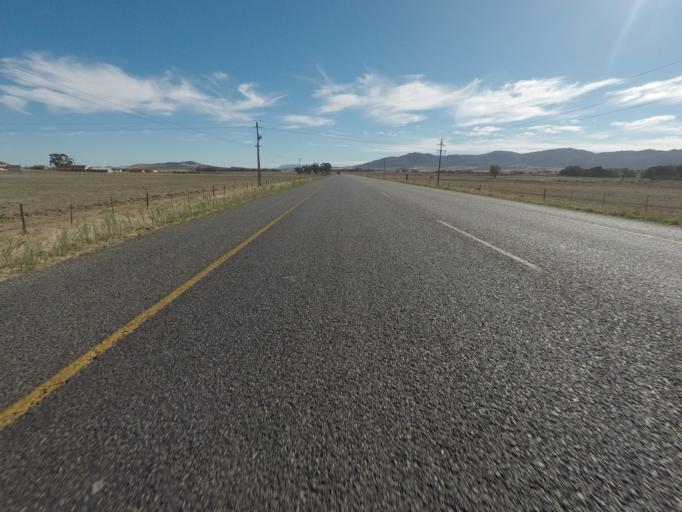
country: ZA
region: Western Cape
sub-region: West Coast District Municipality
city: Malmesbury
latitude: -33.6368
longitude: 18.7187
